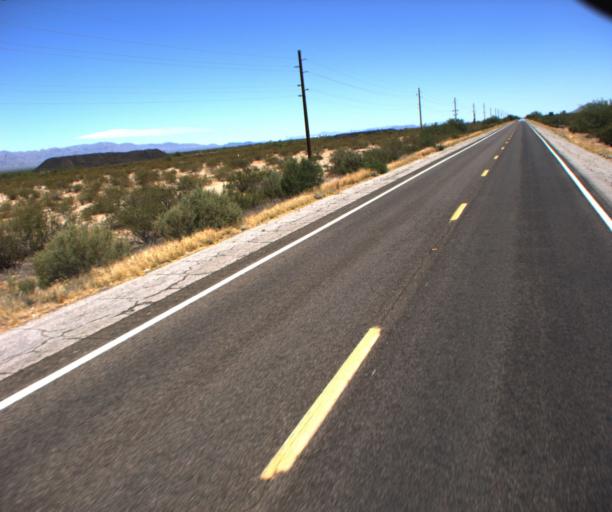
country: US
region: Arizona
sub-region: La Paz County
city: Salome
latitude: 33.8265
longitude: -113.5190
